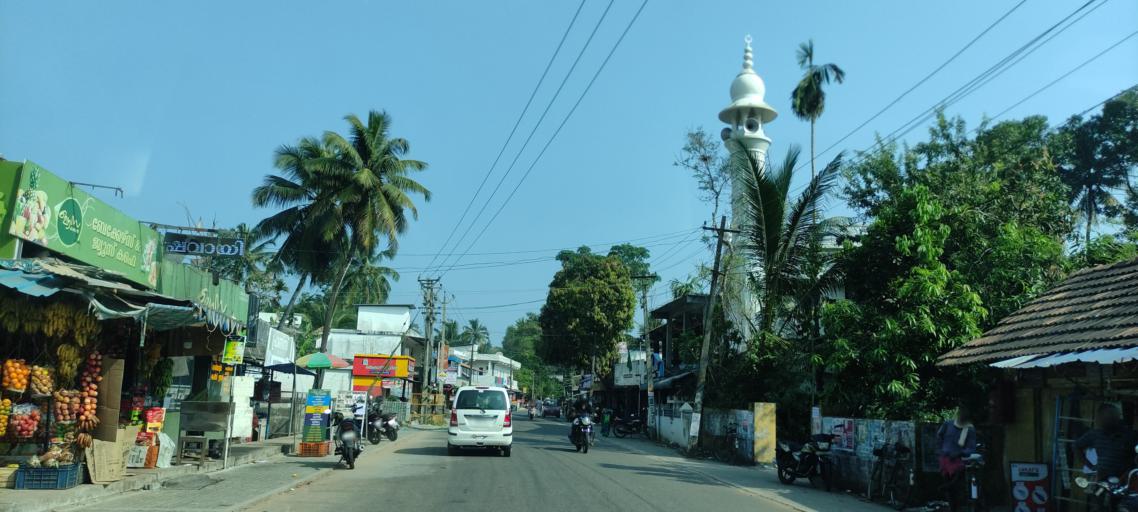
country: IN
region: Kerala
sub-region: Kollam
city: Panmana
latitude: 9.0527
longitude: 76.5603
